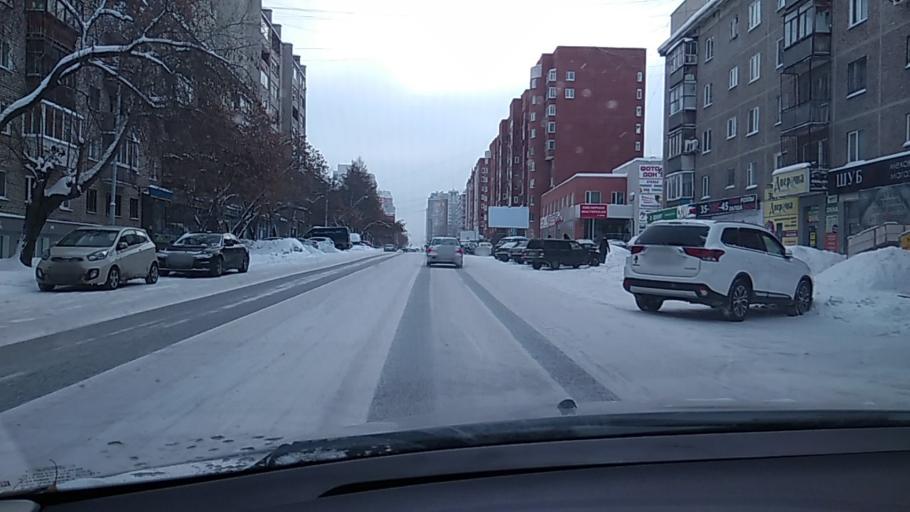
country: RU
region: Sverdlovsk
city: Yekaterinburg
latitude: 56.8119
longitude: 60.6000
